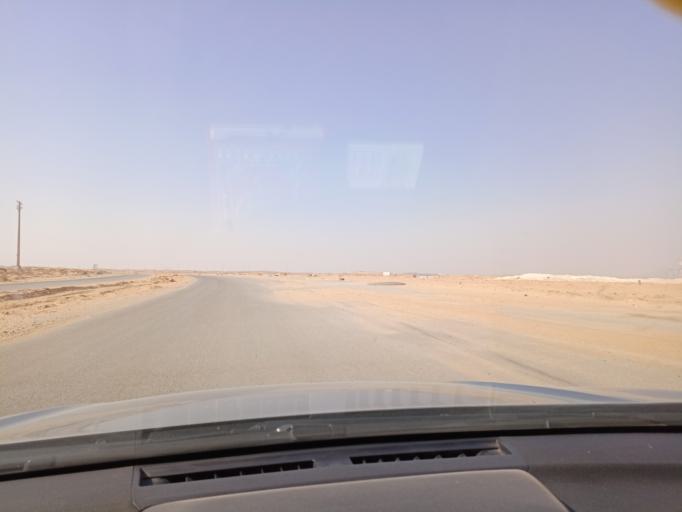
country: EG
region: Muhafazat al Qalyubiyah
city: Al Khankah
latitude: 30.0392
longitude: 31.7161
